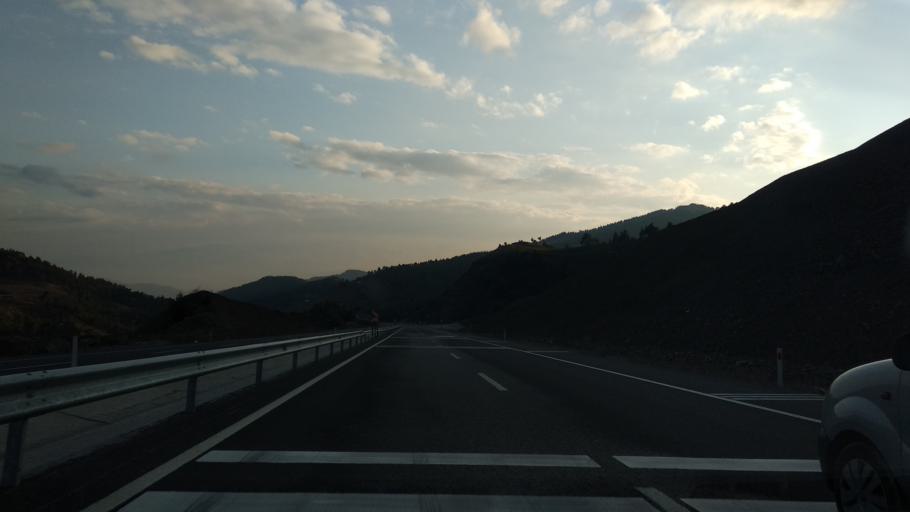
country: TR
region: Kahramanmaras
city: Yenicekale
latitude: 37.7015
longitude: 36.6880
